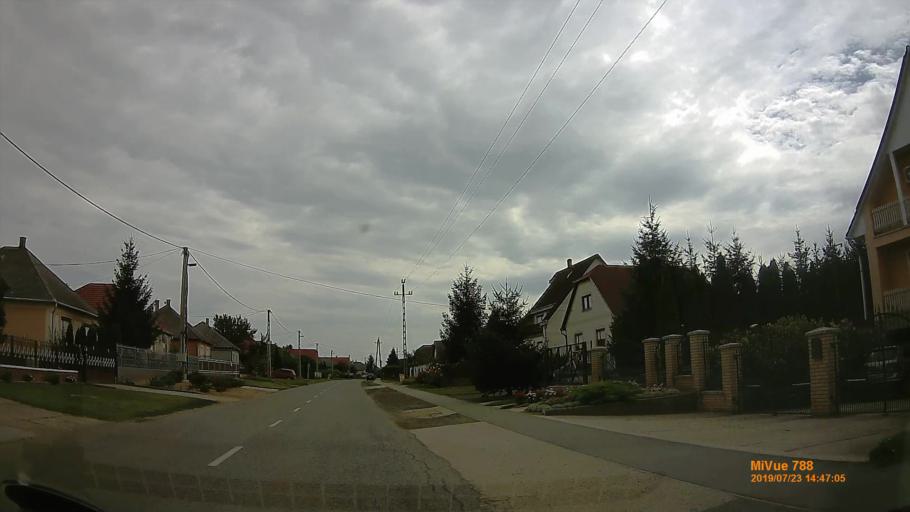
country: HU
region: Szabolcs-Szatmar-Bereg
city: Nyiregyhaza
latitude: 47.9136
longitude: 21.6754
